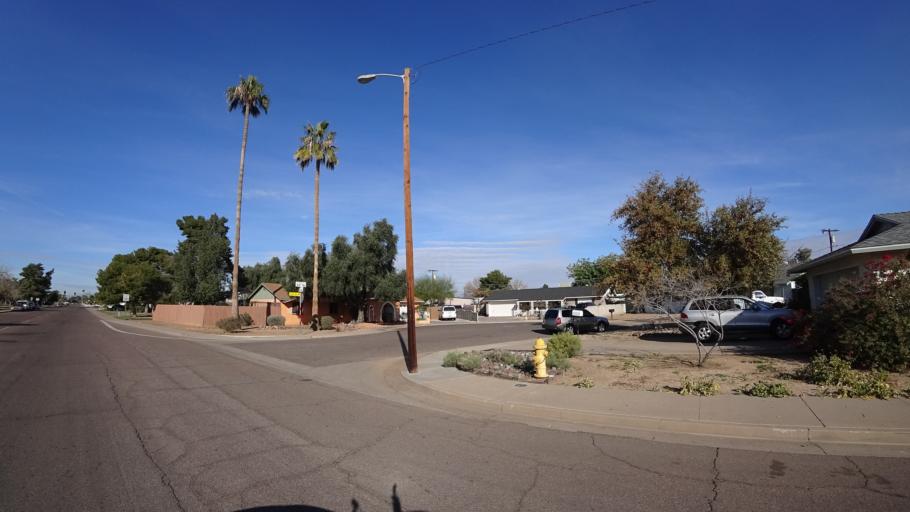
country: US
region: Arizona
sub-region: Maricopa County
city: Glendale
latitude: 33.5603
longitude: -112.1318
